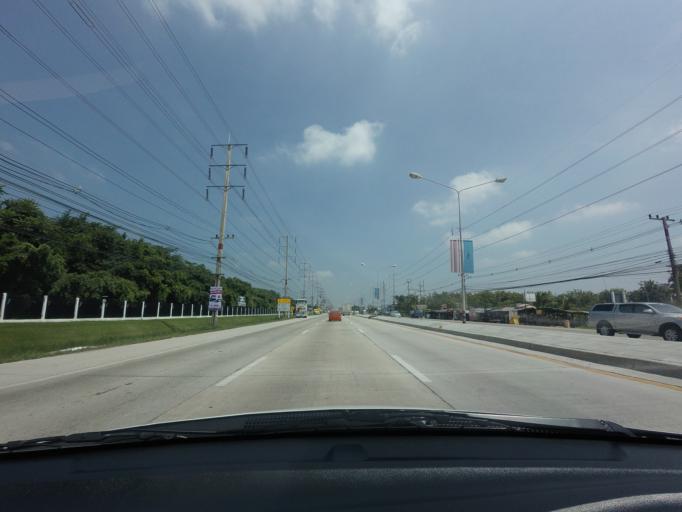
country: TH
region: Chachoengsao
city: Ban Pho
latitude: 13.6135
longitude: 101.0267
